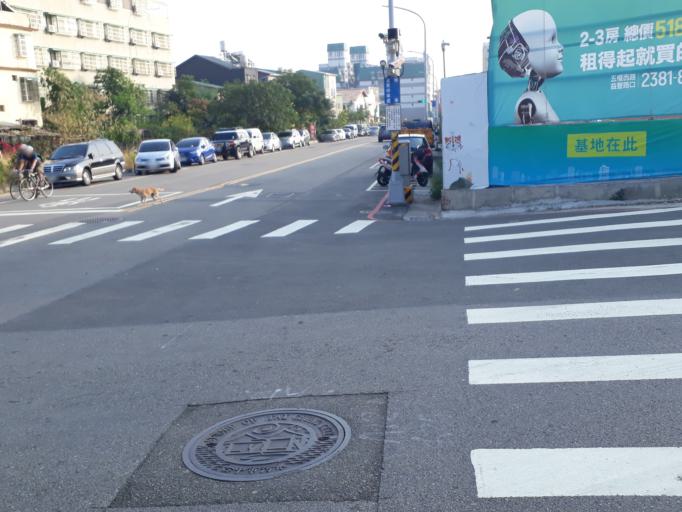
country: TW
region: Taiwan
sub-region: Taichung City
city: Taichung
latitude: 24.1354
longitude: 120.6106
